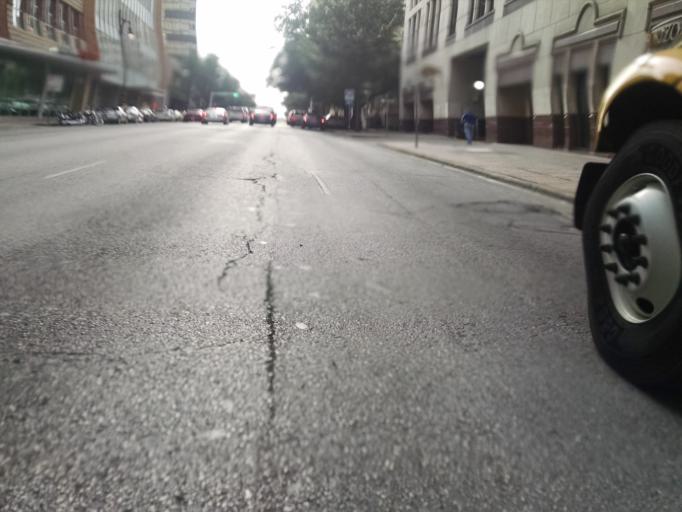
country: US
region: Texas
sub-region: Travis County
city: Austin
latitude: 30.2682
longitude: -97.7430
